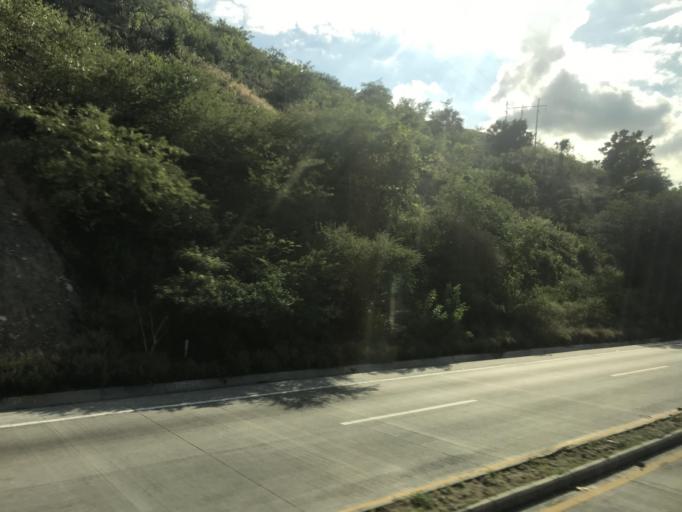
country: GT
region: El Progreso
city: Guastatoya
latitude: 14.8541
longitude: -90.1000
